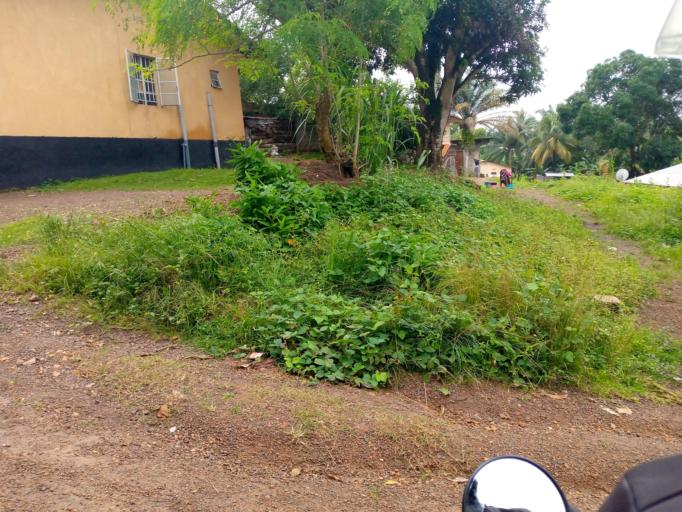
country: SL
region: Eastern Province
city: Kenema
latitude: 7.8601
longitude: -11.1930
